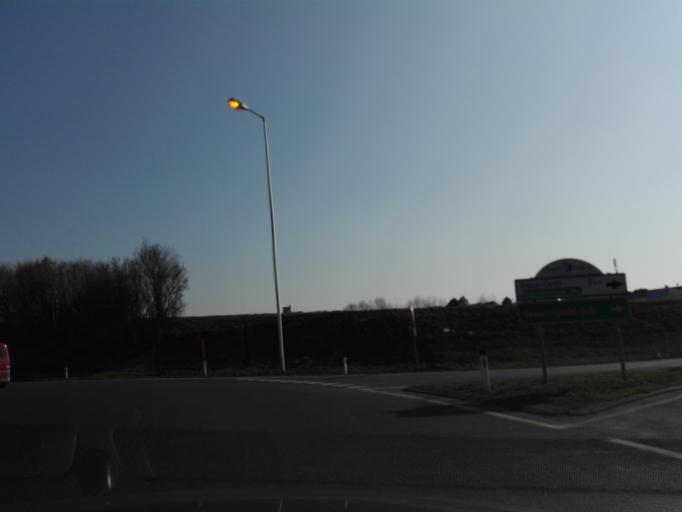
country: AT
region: Upper Austria
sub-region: Politischer Bezirk Linz-Land
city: Traun
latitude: 48.2237
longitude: 14.2249
